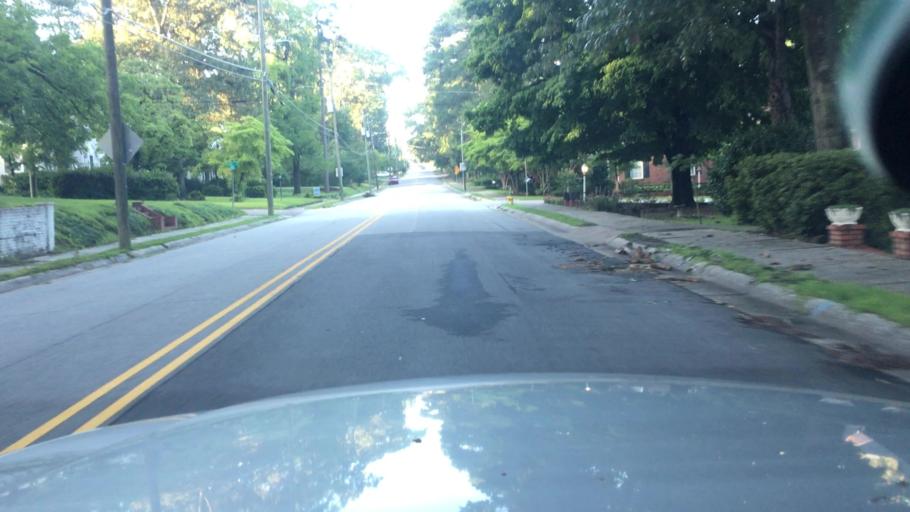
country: US
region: North Carolina
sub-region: Cumberland County
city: Fayetteville
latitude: 35.0645
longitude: -78.9050
